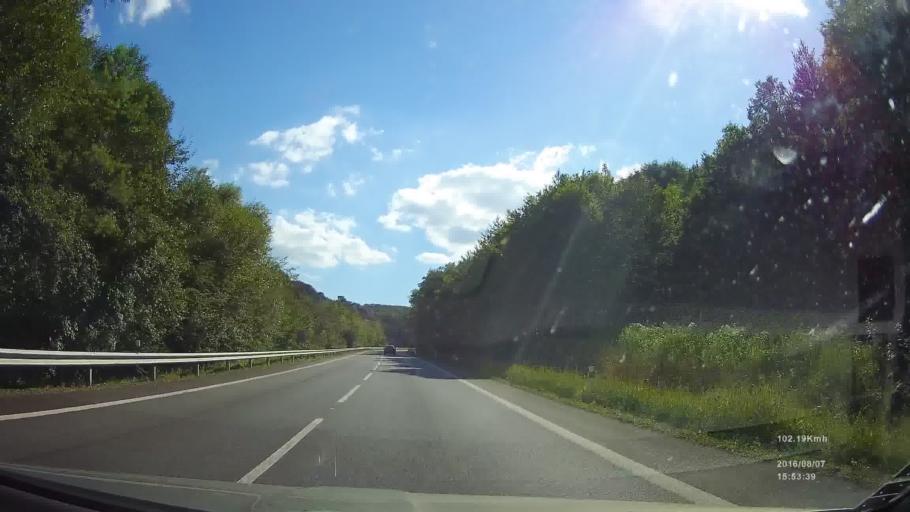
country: SK
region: Presovsky
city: Giraltovce
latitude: 49.0968
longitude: 21.4502
